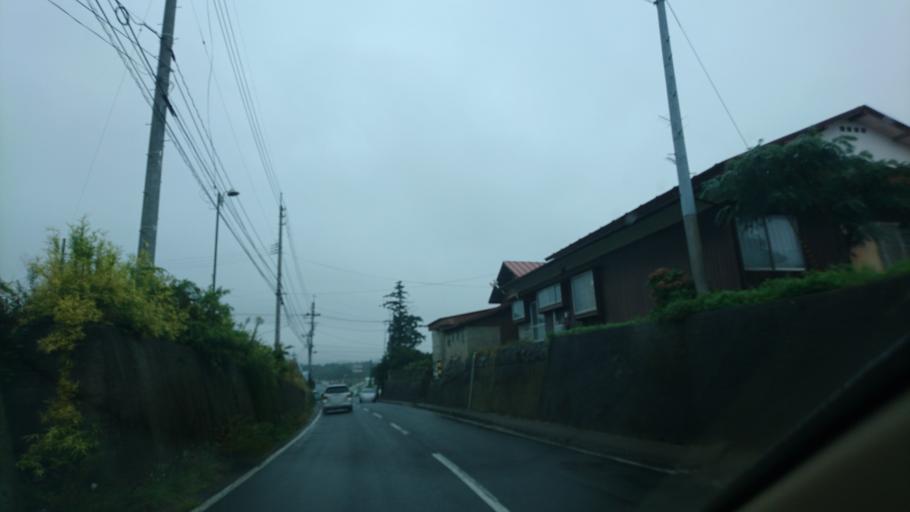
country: JP
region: Iwate
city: Mizusawa
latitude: 39.1356
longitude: 141.1658
